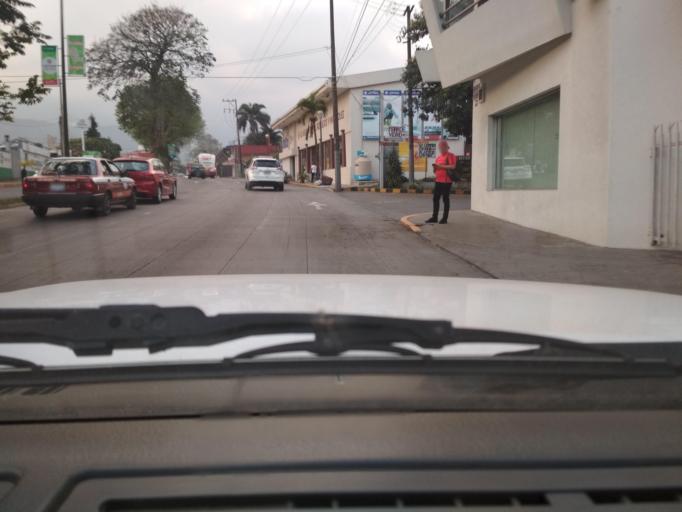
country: MX
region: Veracruz
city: Orizaba
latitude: 18.8583
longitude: -97.0901
